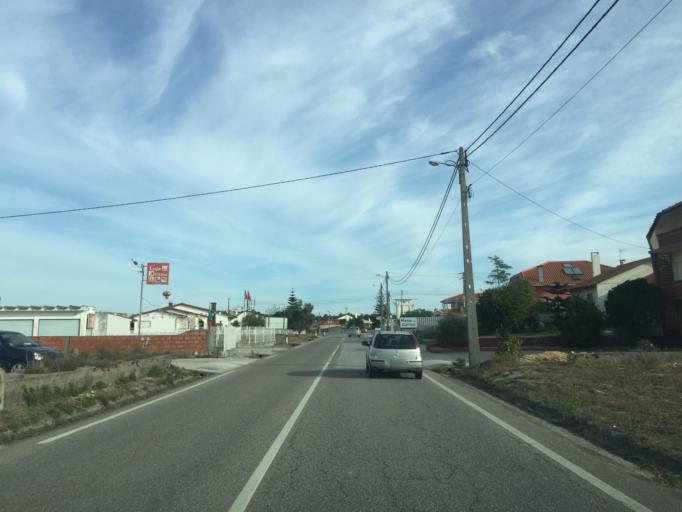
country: PT
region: Leiria
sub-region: Pombal
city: Lourical
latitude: 39.9793
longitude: -8.7989
